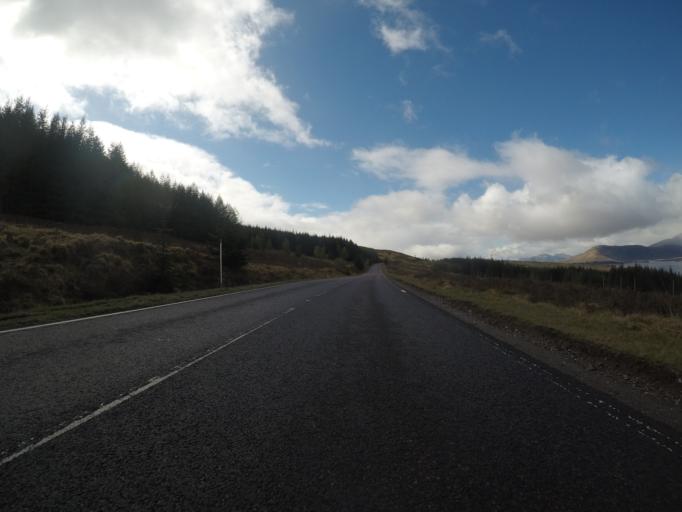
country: GB
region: Scotland
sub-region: Highland
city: Spean Bridge
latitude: 57.1067
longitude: -4.9851
